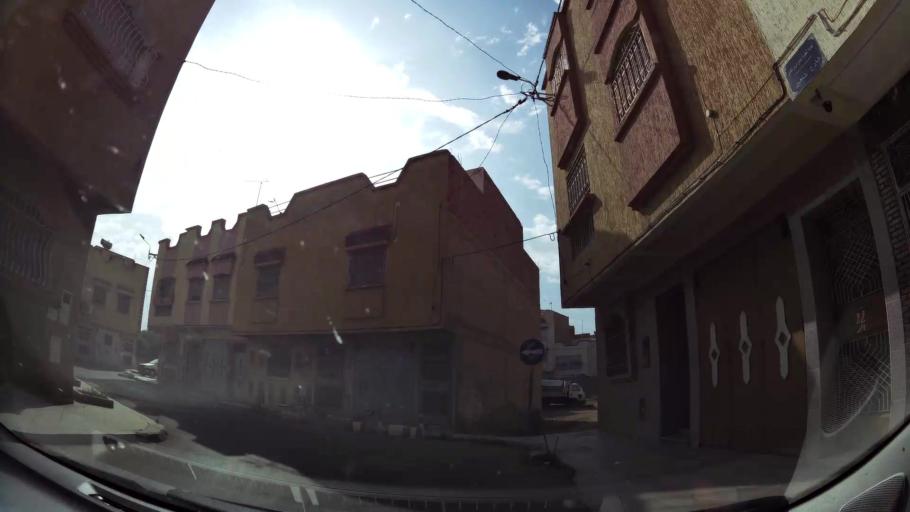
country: MA
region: Oriental
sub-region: Oujda-Angad
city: Oujda
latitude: 34.6937
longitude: -1.9018
